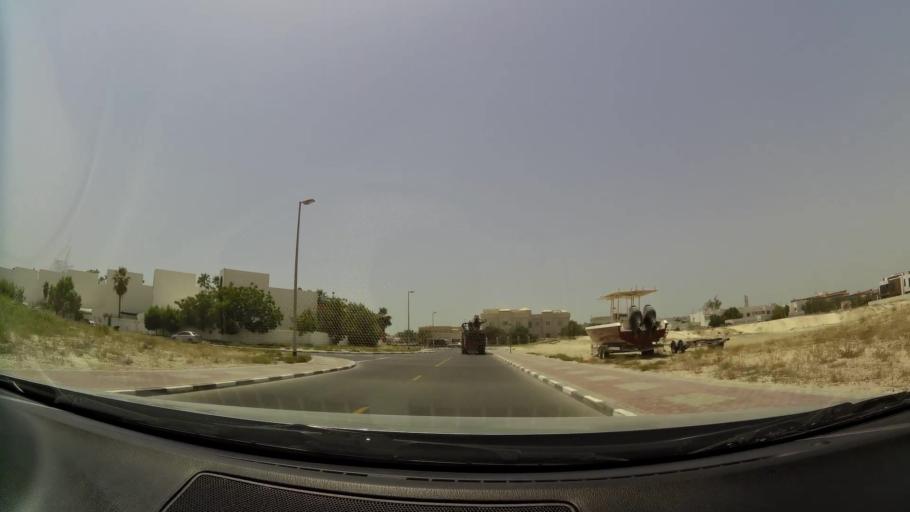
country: AE
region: Dubai
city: Dubai
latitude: 25.1460
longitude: 55.2017
